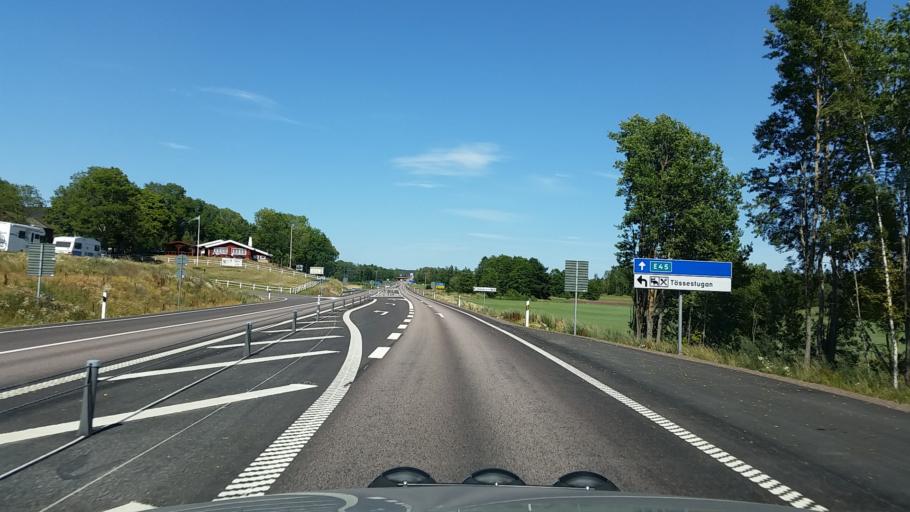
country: SE
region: Vaestra Goetaland
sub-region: Amals Kommun
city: Amal
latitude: 58.9645
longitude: 12.6137
